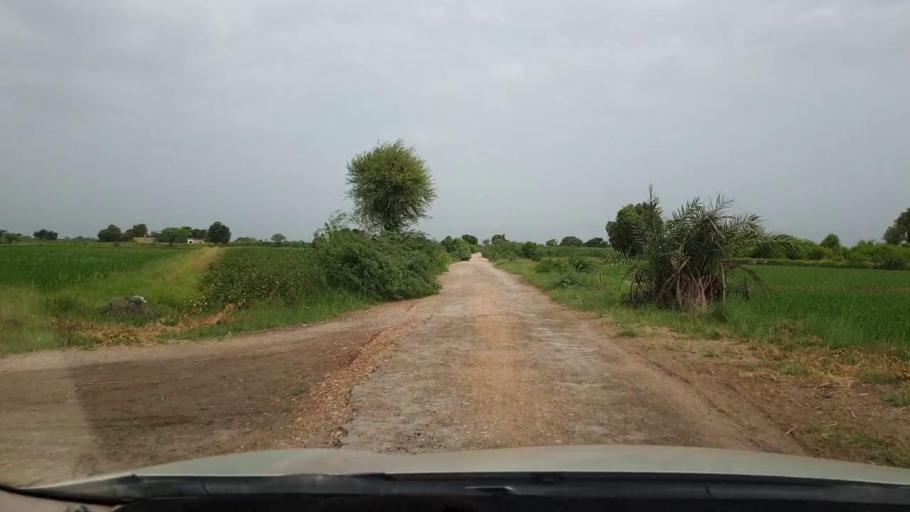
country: PK
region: Sindh
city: Matli
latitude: 25.1063
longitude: 68.6155
